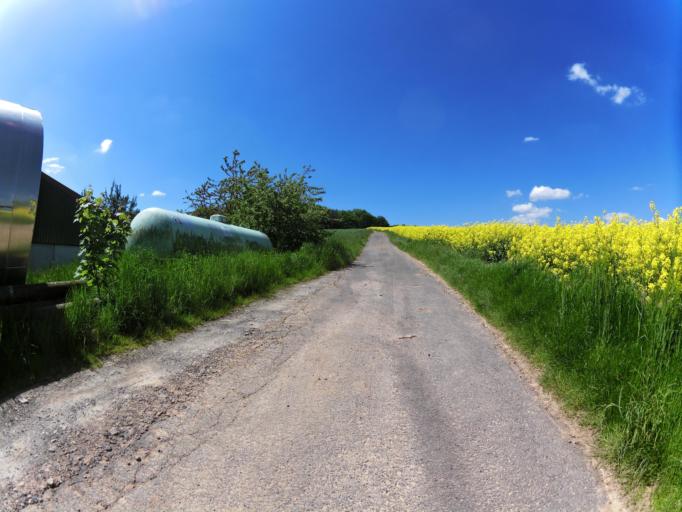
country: DE
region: Thuringia
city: Dankmarshausen
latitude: 50.9617
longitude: 9.9955
